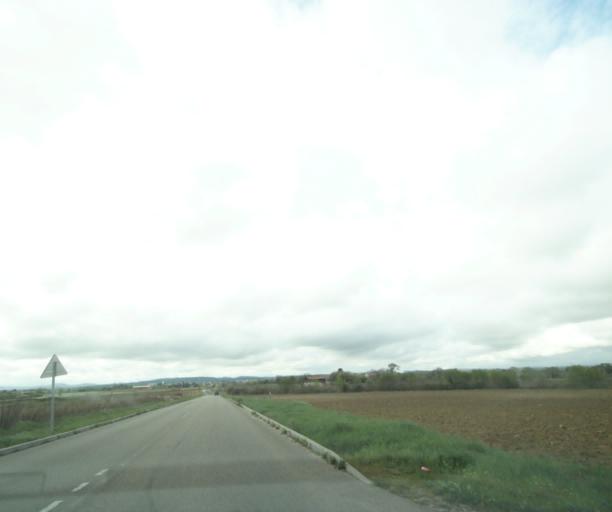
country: FR
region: Languedoc-Roussillon
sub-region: Departement de l'Herault
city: Fabregues
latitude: 43.5618
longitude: 3.7943
